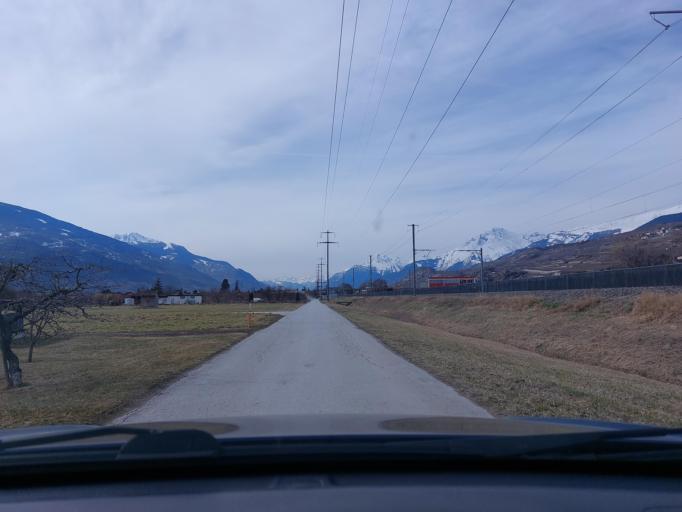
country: CH
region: Valais
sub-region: Sion District
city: Saint-Leonard
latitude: 46.2545
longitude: 7.4292
